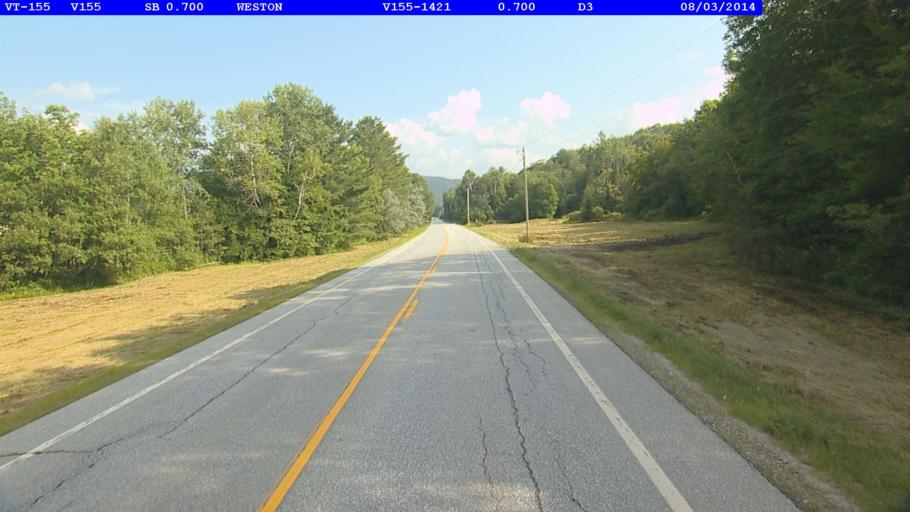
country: US
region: Vermont
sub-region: Windsor County
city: Chester
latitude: 43.3463
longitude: -72.7902
